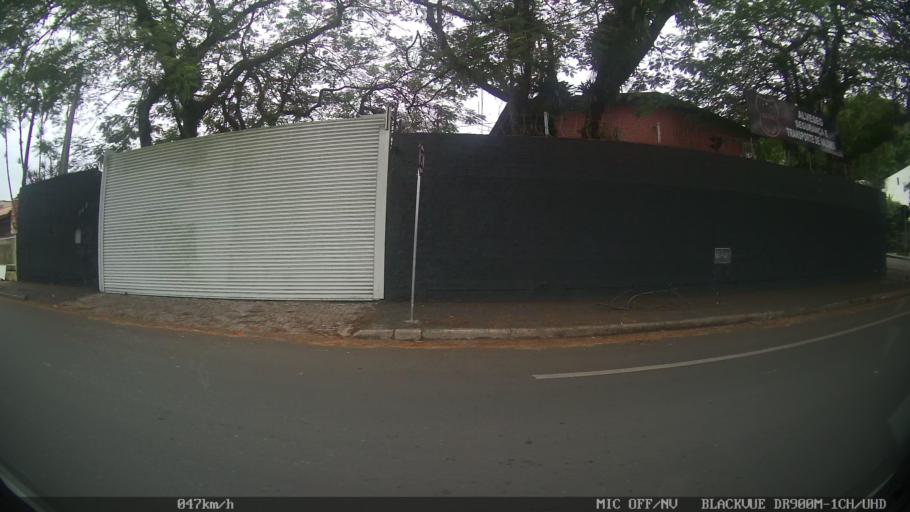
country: BR
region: Santa Catarina
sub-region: Joinville
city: Joinville
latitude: -26.3269
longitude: -48.8495
